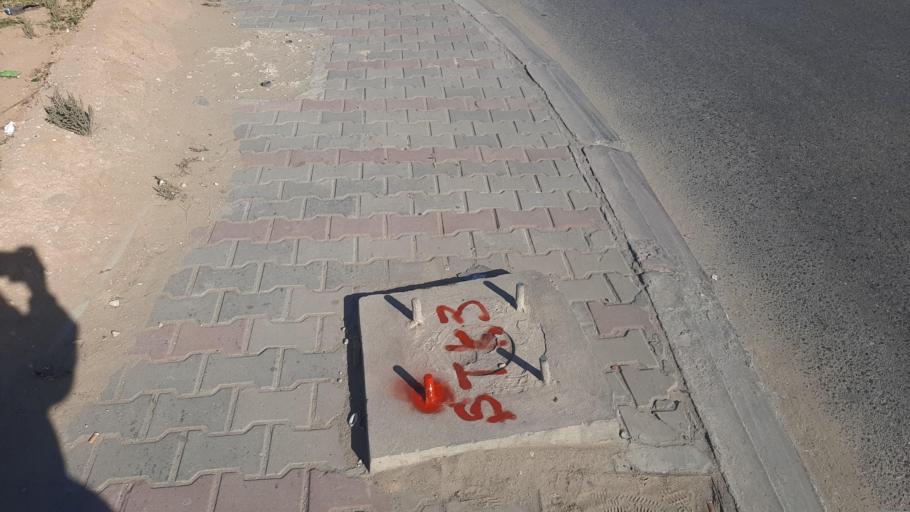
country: TN
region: Qabis
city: Gabes
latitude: 33.8699
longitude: 10.1095
